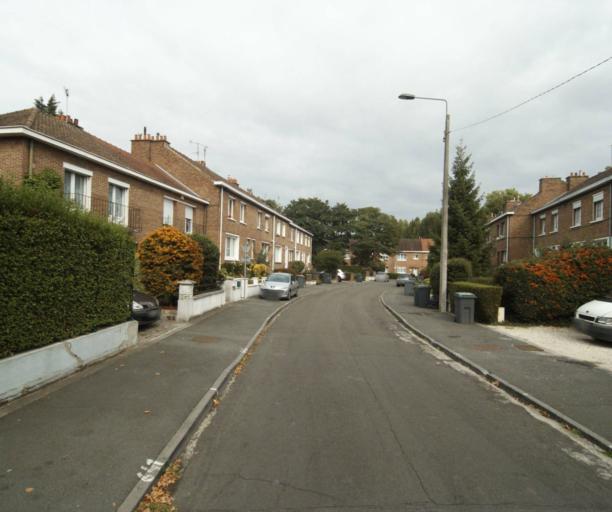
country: FR
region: Nord-Pas-de-Calais
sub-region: Departement du Nord
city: Lambersart
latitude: 50.6416
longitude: 3.0334
